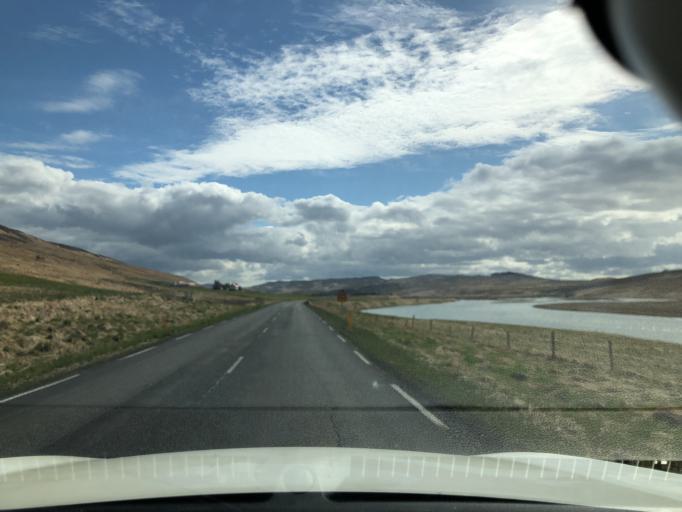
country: IS
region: Northwest
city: Saudarkrokur
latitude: 65.6112
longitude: -20.1261
